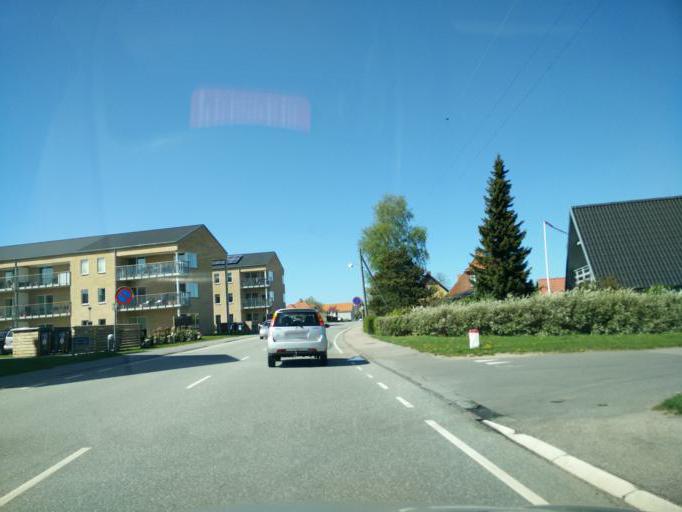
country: DK
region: Capital Region
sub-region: Gribskov Kommune
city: Helsinge
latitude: 56.0169
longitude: 12.2027
